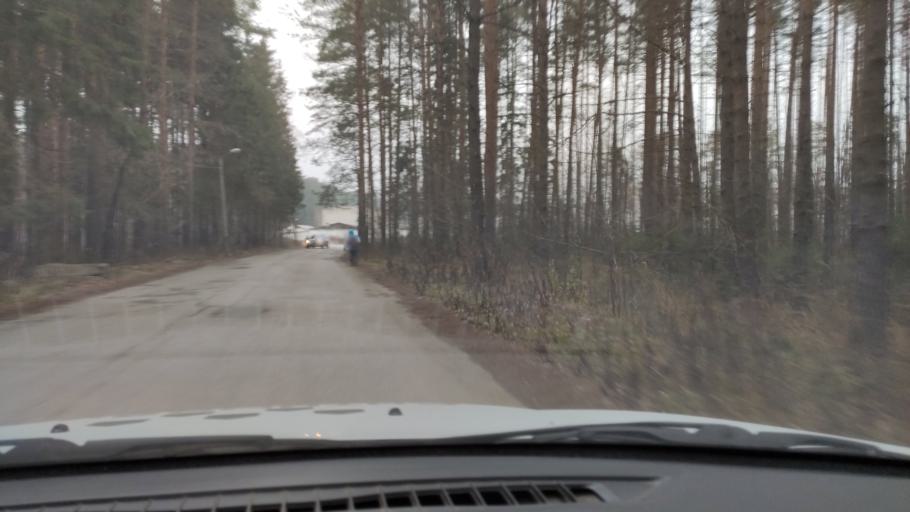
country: RU
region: Perm
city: Kondratovo
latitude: 58.0419
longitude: 56.1382
